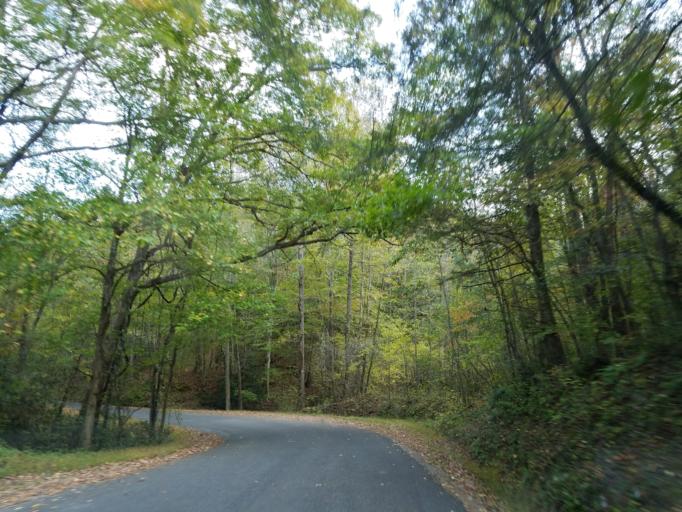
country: US
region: Georgia
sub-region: Gilmer County
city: Ellijay
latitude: 34.6310
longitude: -84.2632
